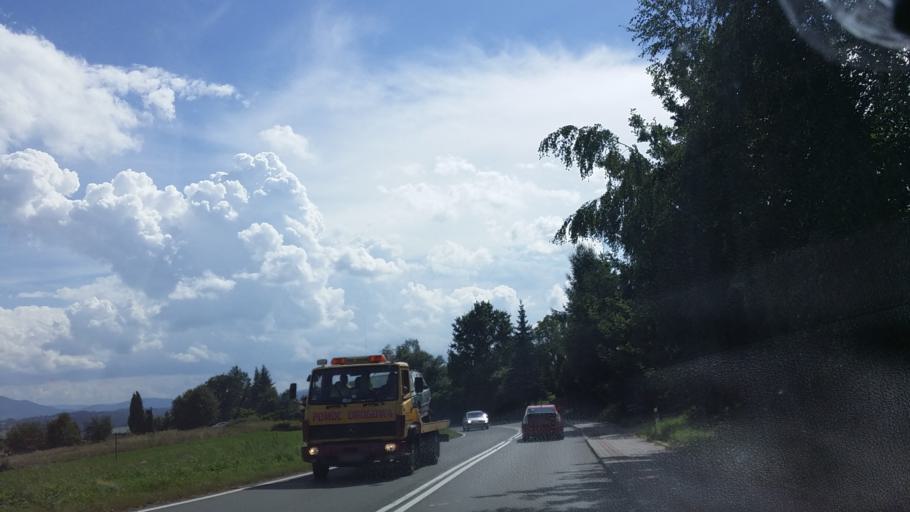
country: PL
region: Lesser Poland Voivodeship
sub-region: Powiat myslenicki
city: Dobczyce
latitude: 49.9071
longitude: 20.0976
